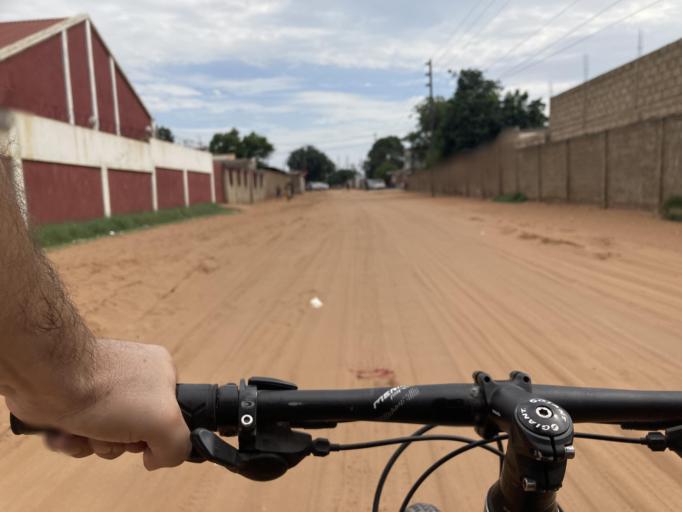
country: MZ
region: Maputo City
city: Maputo
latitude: -25.8949
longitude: 32.6074
